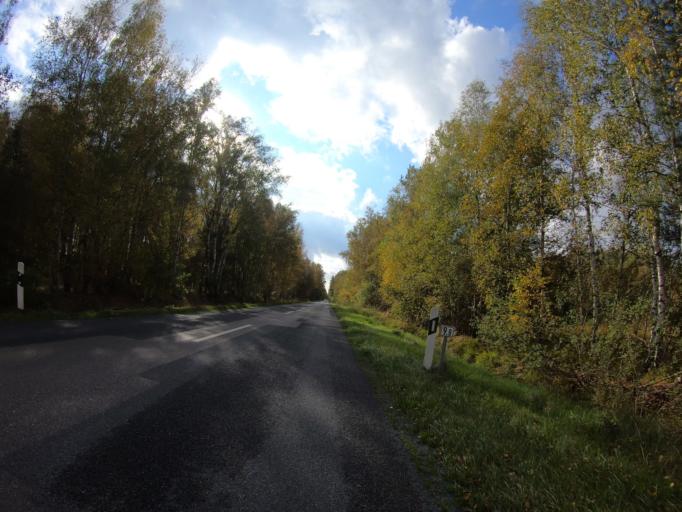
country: DE
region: Lower Saxony
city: Wahrenholz
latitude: 52.5745
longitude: 10.6354
